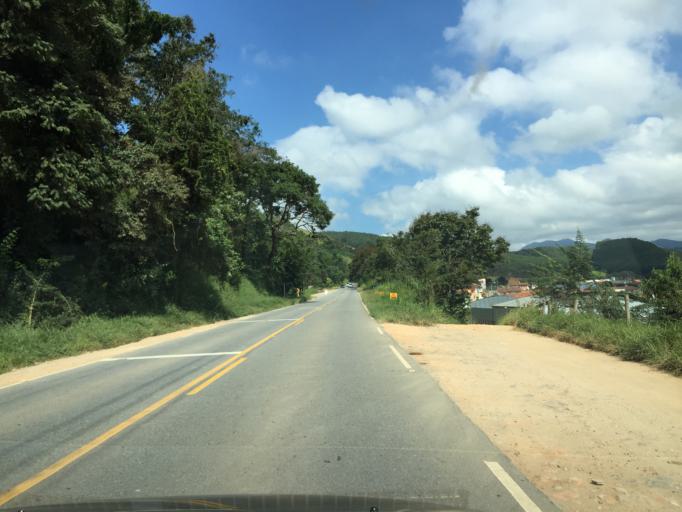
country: BR
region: Minas Gerais
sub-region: Passa Quatro
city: Passa Quatro
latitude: -22.3917
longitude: -44.9626
